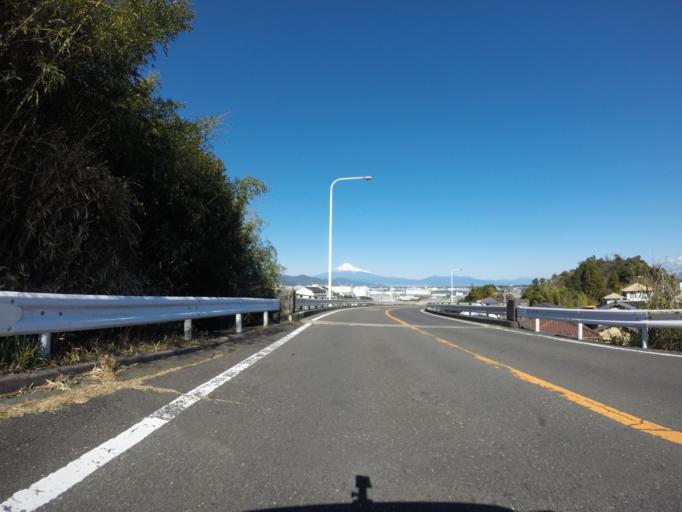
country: JP
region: Shizuoka
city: Shizuoka-shi
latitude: 34.9792
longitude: 138.4892
